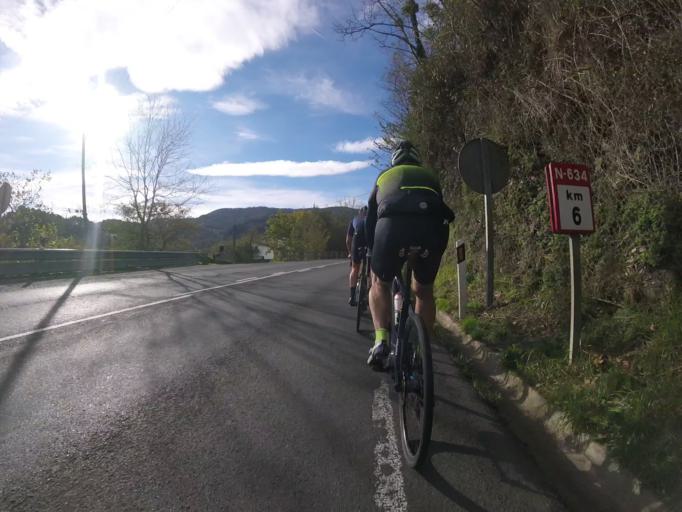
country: ES
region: Basque Country
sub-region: Provincia de Guipuzcoa
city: Usurbil
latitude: 43.2738
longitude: -2.0674
